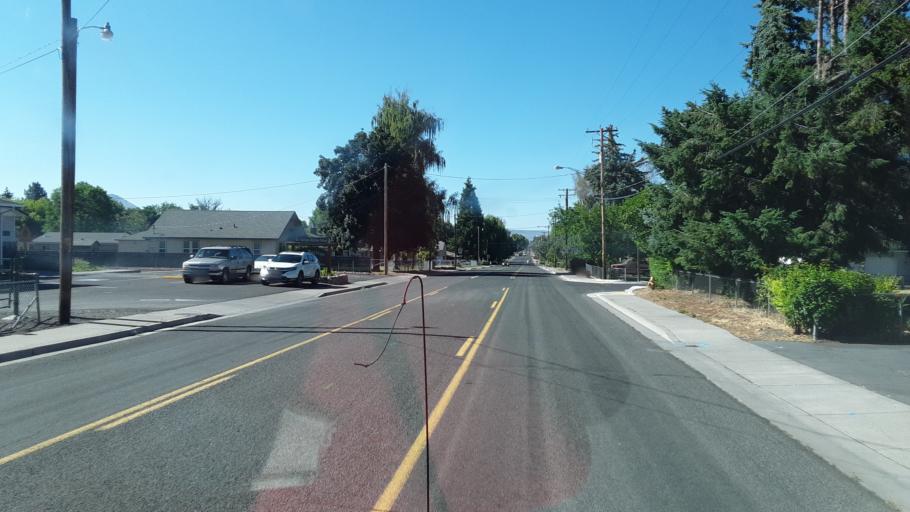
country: US
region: Oregon
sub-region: Klamath County
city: Altamont
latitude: 42.2114
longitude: -121.7227
